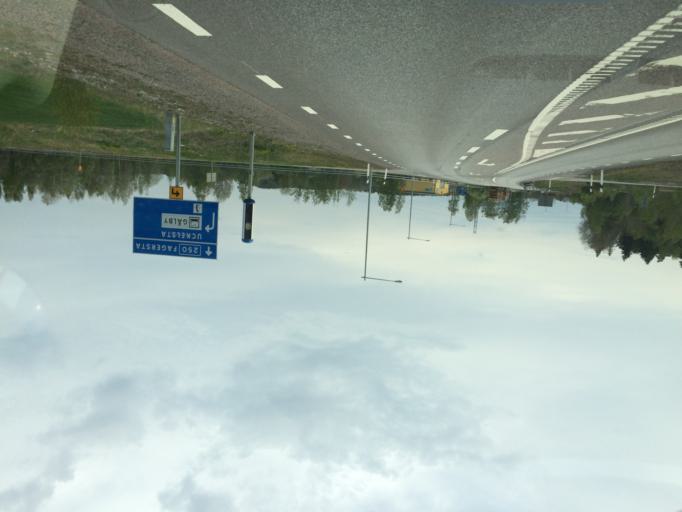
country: SE
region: Vaestmanland
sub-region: Kopings Kommun
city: Koping
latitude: 59.5348
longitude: 15.9543
